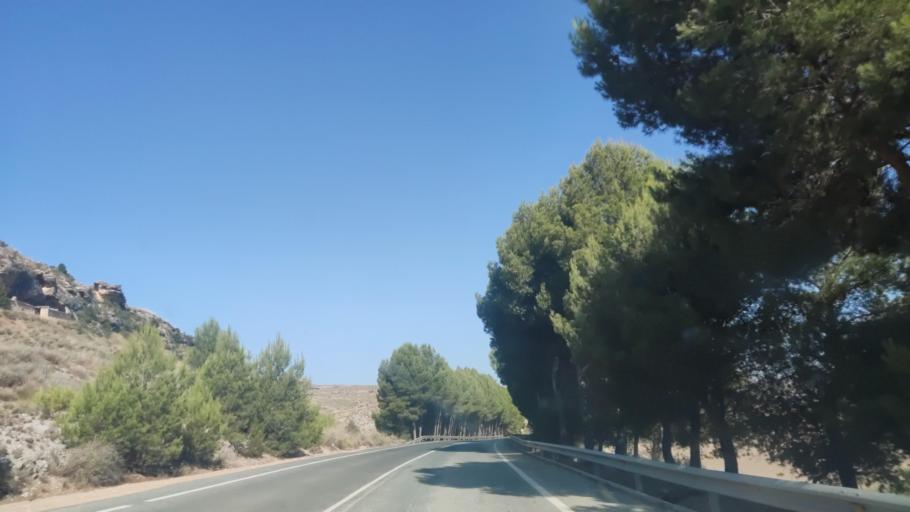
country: ES
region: Castille-La Mancha
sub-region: Provincia de Albacete
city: Hellin
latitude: 38.4780
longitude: -1.6059
